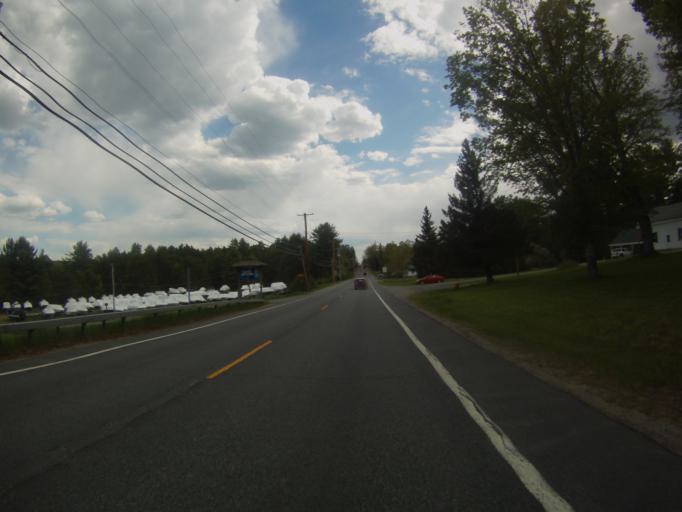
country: US
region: New York
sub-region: Essex County
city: Ticonderoga
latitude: 43.8475
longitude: -73.7584
